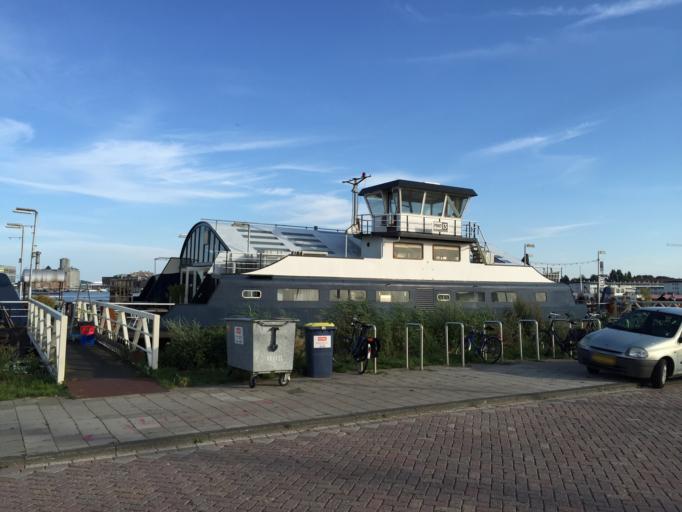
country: NL
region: North Holland
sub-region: Gemeente Amsterdam
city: Amsterdam
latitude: 52.3979
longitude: 4.8830
